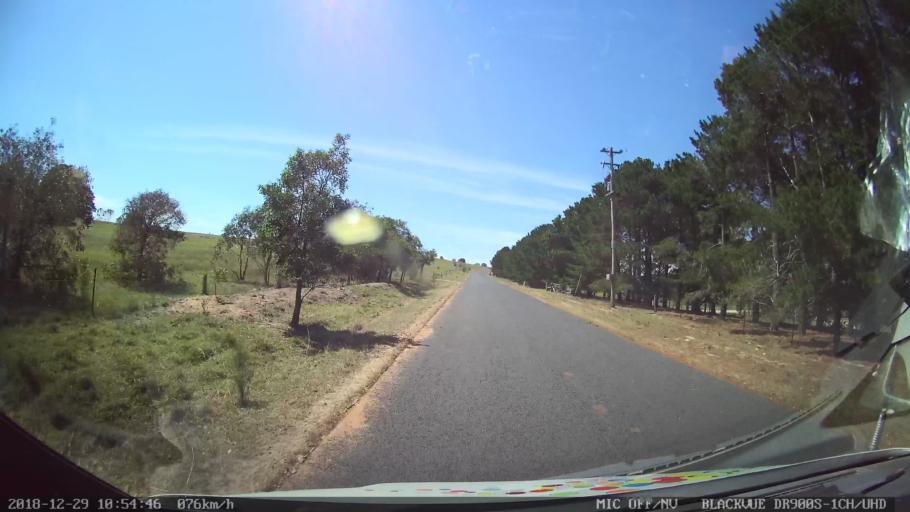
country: AU
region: New South Wales
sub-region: Palerang
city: Bungendore
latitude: -35.1176
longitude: 149.5292
